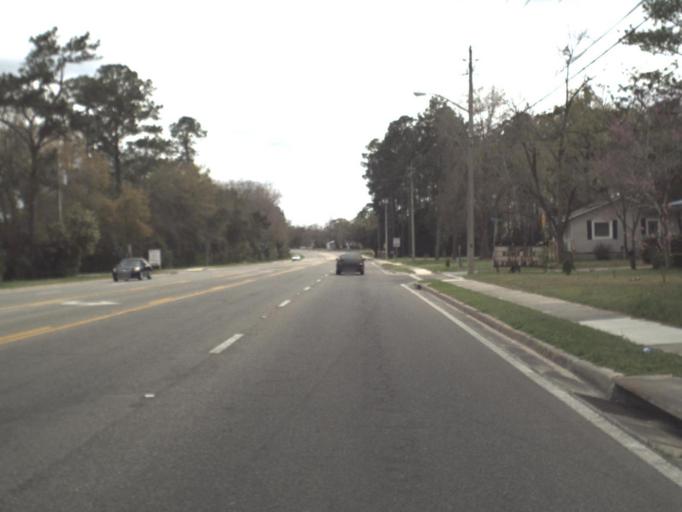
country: US
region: Florida
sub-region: Gadsden County
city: Quincy
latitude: 30.5716
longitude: -84.5932
